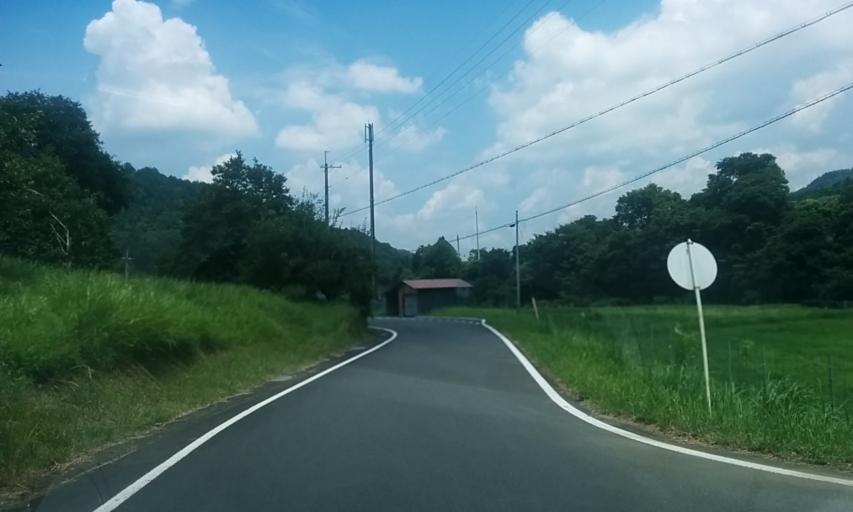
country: JP
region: Kyoto
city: Ayabe
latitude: 35.1916
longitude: 135.2169
